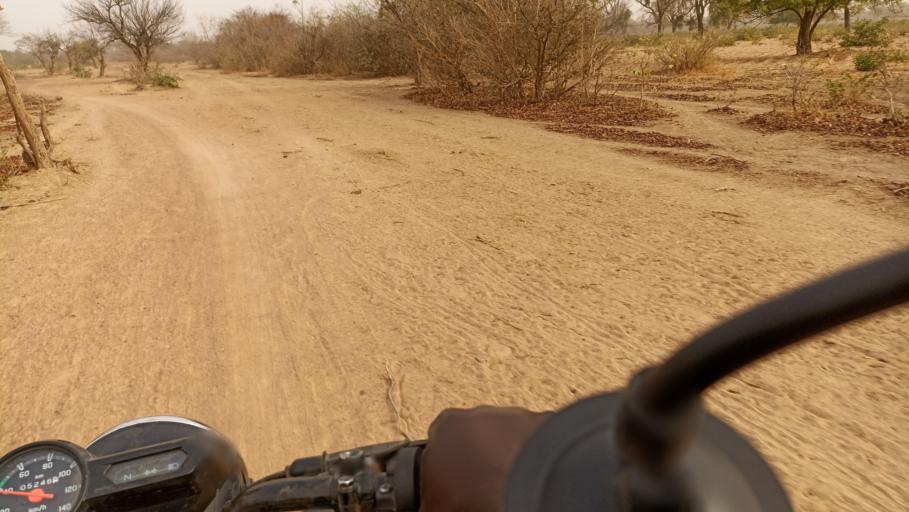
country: BF
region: Boucle du Mouhoun
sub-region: Province du Nayala
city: Toma
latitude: 12.8689
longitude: -2.7522
